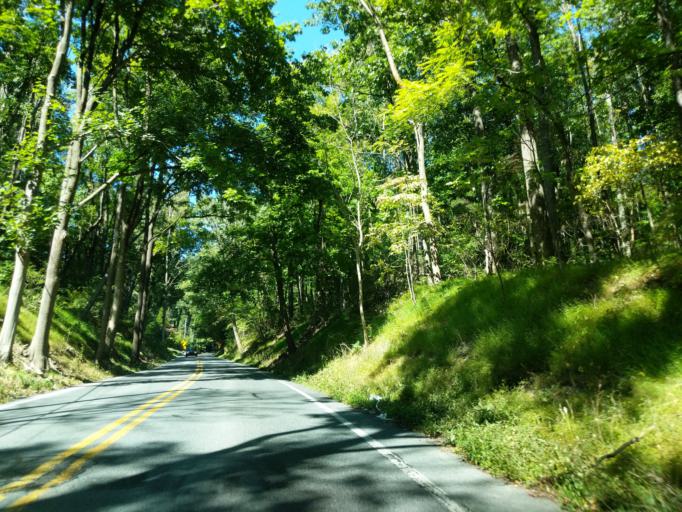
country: US
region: Pennsylvania
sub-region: Montgomery County
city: East Greenville
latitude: 40.4413
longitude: -75.4867
